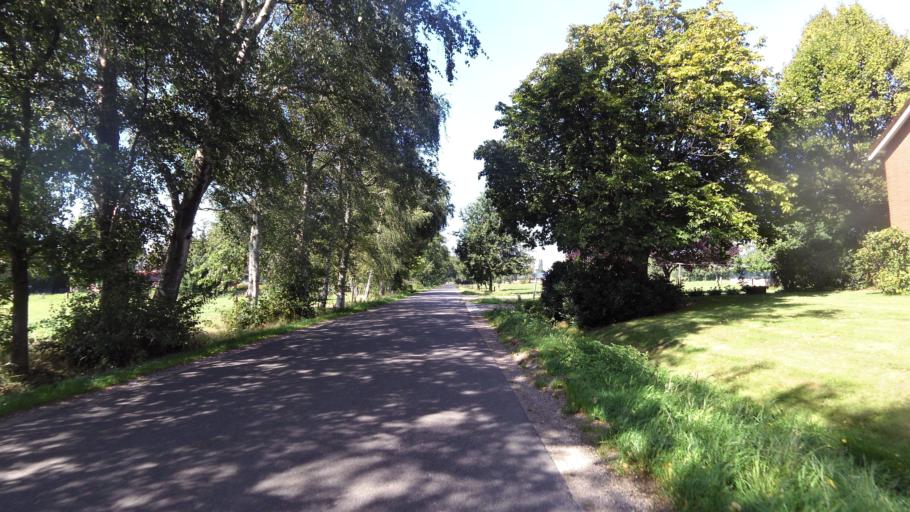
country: NL
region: Gelderland
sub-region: Gemeente Ede
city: Harskamp
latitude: 52.1133
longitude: 5.7548
